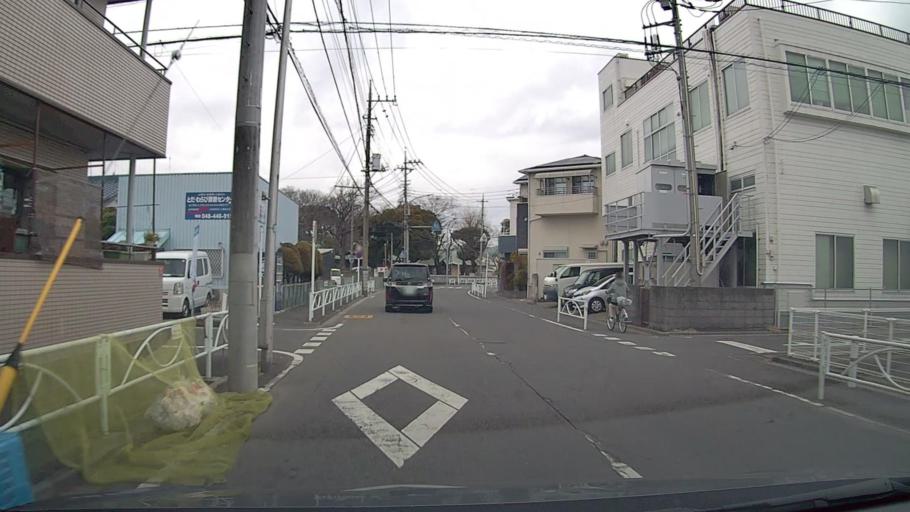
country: JP
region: Saitama
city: Shimotoda
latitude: 35.8097
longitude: 139.6574
